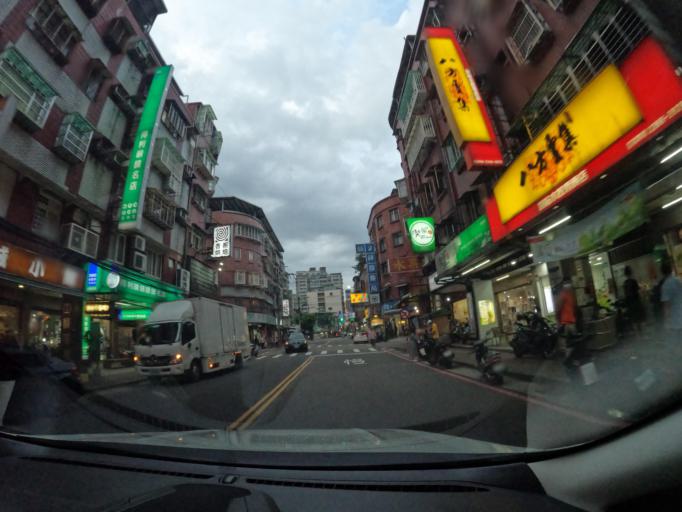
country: TW
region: Taipei
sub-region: Taipei
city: Banqiao
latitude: 24.9806
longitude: 121.4591
